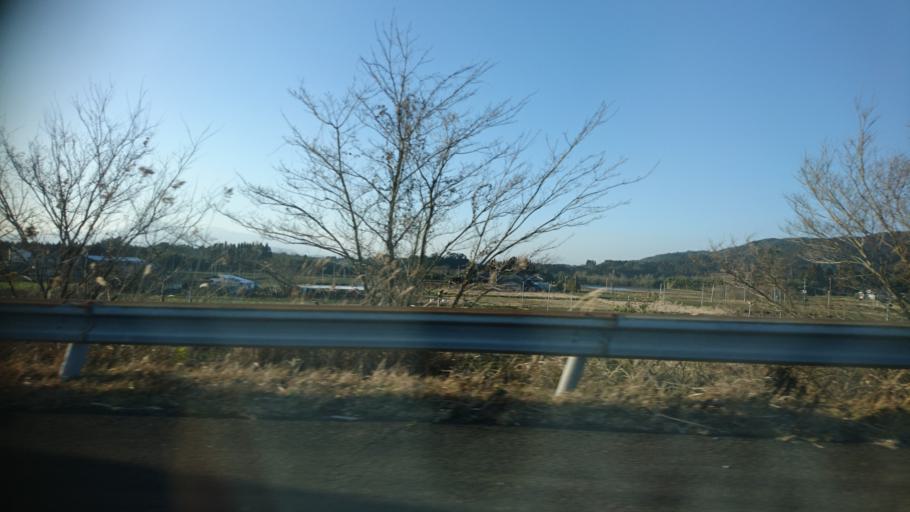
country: JP
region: Miyazaki
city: Miyakonojo
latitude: 31.7920
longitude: 131.1557
